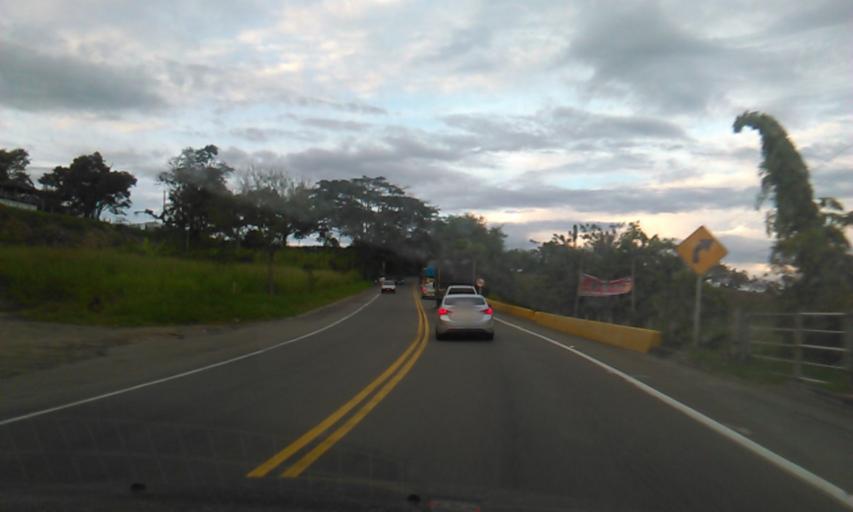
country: CO
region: Quindio
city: La Tebaida
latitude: 4.4306
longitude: -75.8605
